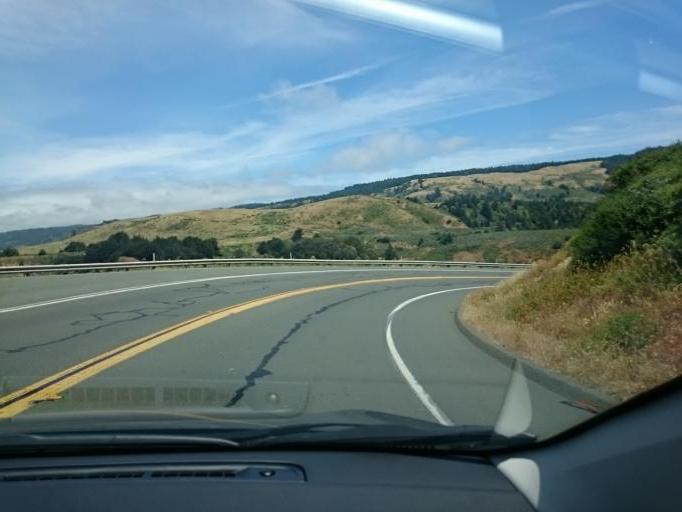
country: US
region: California
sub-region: Mendocino County
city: Boonville
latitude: 39.1000
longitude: -123.7069
